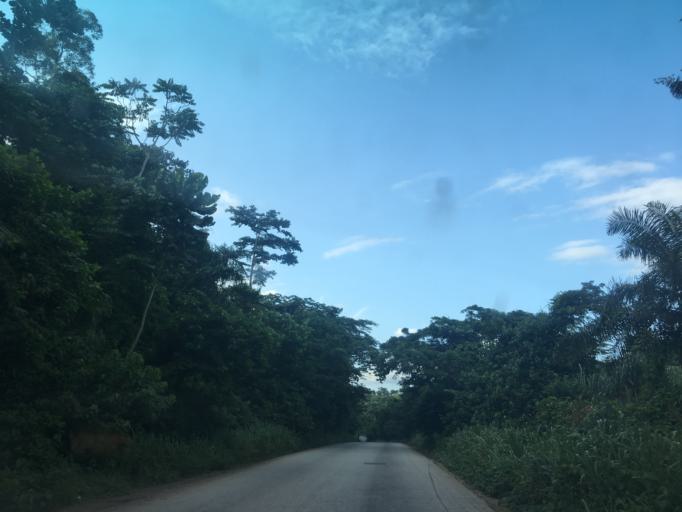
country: GH
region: Western
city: Bibiani
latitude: 6.2775
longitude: -2.2258
